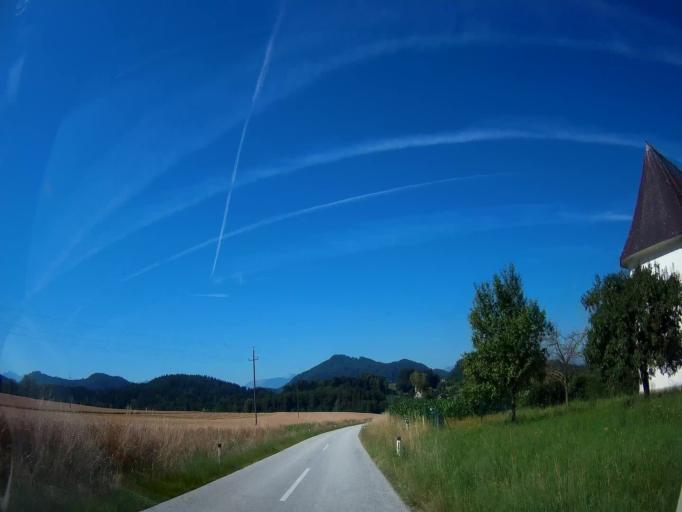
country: AT
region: Carinthia
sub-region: Politischer Bezirk Klagenfurt Land
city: Maria Saal
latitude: 46.6937
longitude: 14.3666
